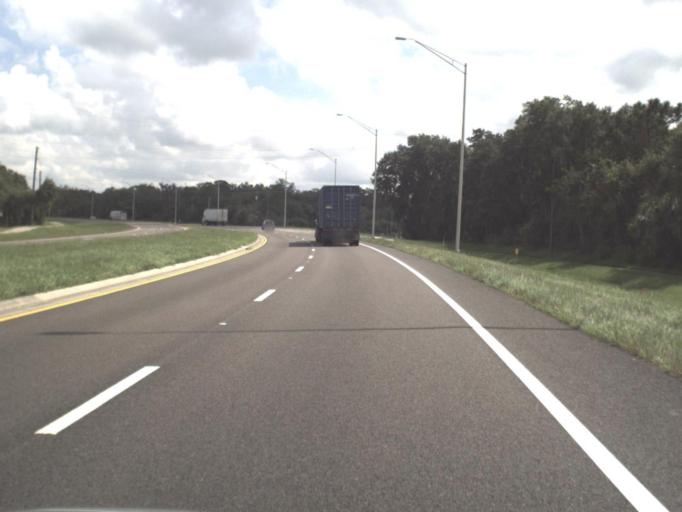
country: US
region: Florida
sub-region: Manatee County
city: Ellenton
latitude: 27.4772
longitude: -82.4022
